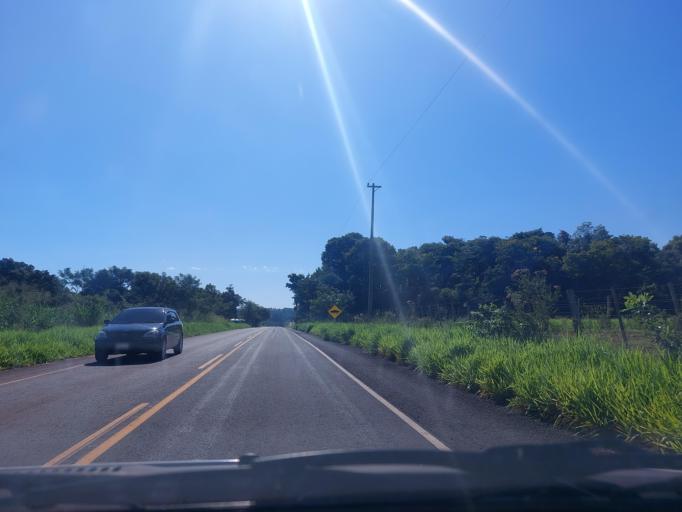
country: PY
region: San Pedro
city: Guayaybi
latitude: -24.3020
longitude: -56.1454
